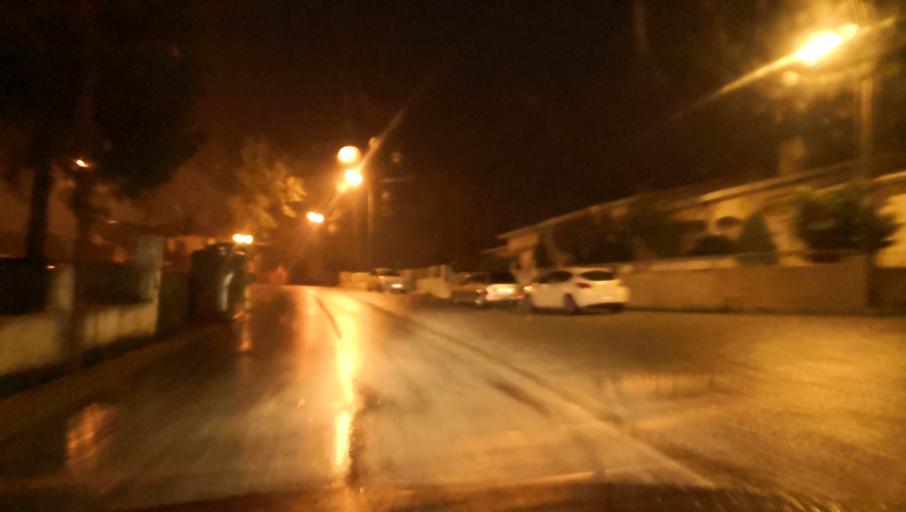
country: PT
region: Vila Real
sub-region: Vila Real
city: Vila Real
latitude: 41.3380
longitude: -7.7241
